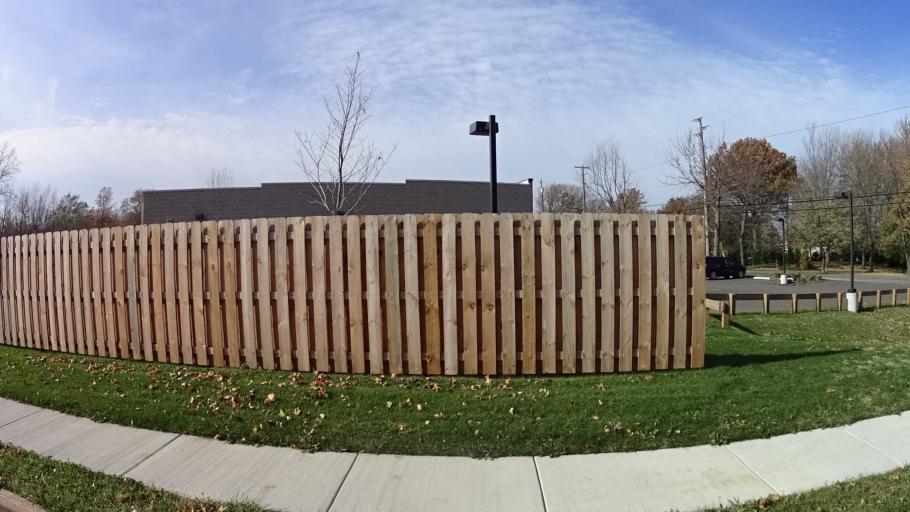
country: US
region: Ohio
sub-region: Lorain County
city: Sheffield Lake
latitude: 41.4935
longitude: -82.0944
